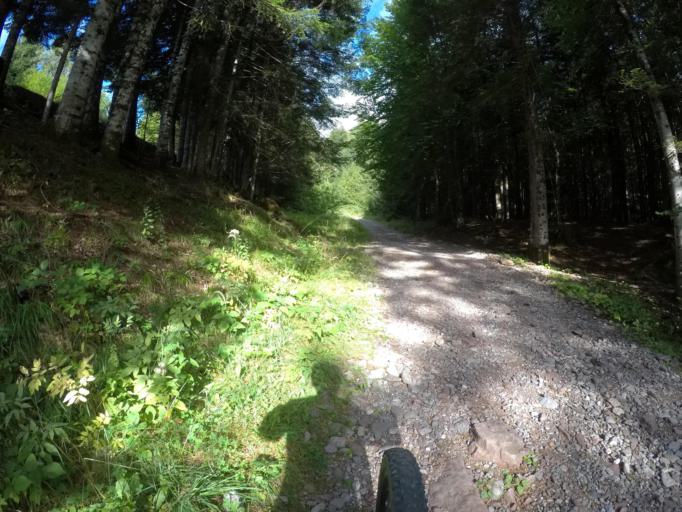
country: IT
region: Friuli Venezia Giulia
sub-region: Provincia di Udine
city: Paularo
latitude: 46.5420
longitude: 13.1089
